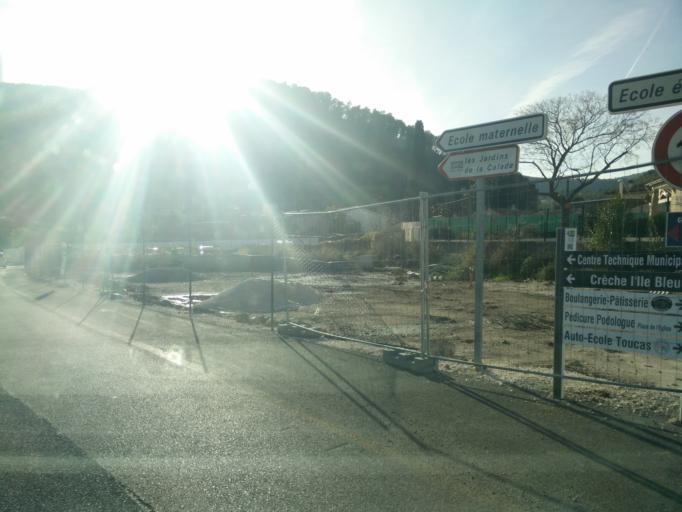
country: FR
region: Provence-Alpes-Cote d'Azur
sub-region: Departement du Var
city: Sollies-Toucas
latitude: 43.2042
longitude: 6.0258
